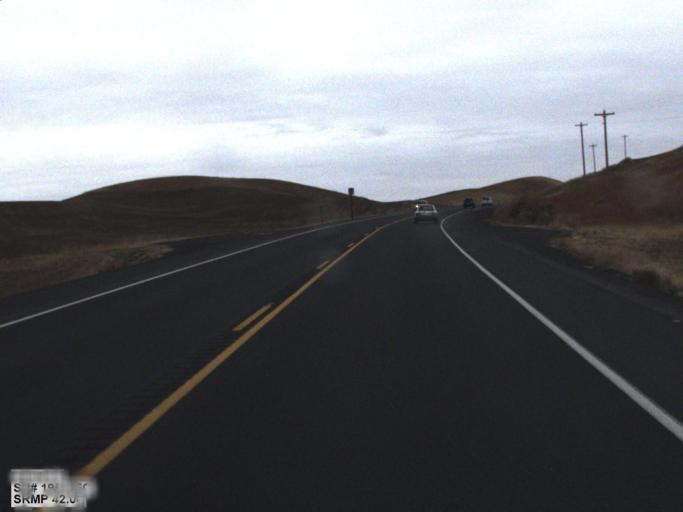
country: US
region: Washington
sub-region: Whitman County
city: Colfax
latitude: 46.9322
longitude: -117.3364
